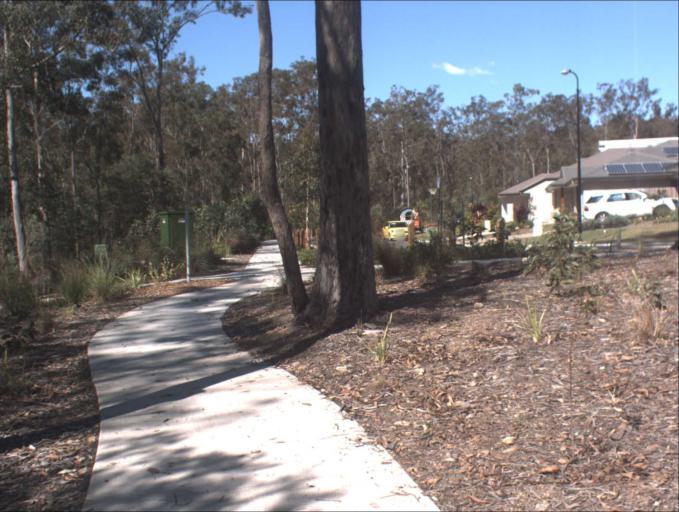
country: AU
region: Queensland
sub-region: Logan
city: Waterford West
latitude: -27.7150
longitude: 153.1531
